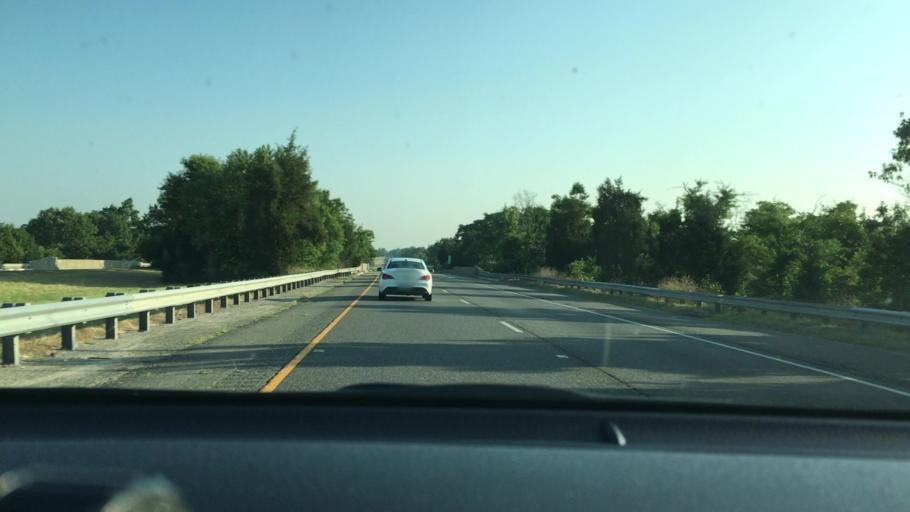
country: US
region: New Jersey
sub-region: Cumberland County
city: Vineland
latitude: 39.4945
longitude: -75.0701
